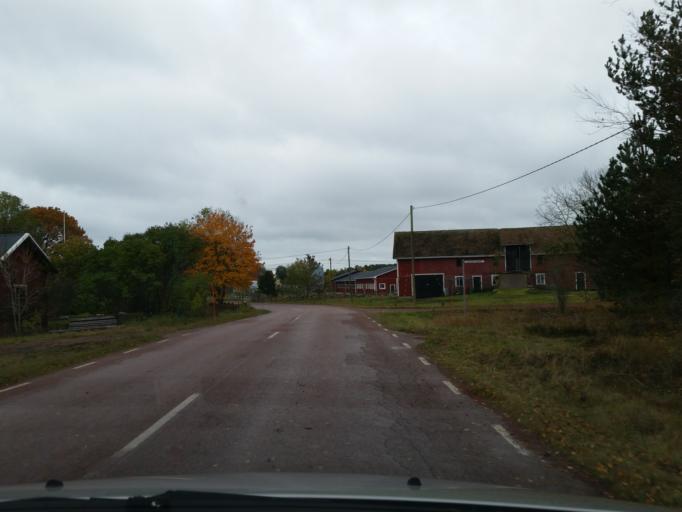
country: AX
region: Alands landsbygd
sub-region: Lumparland
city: Lumparland
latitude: 60.1236
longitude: 20.2410
